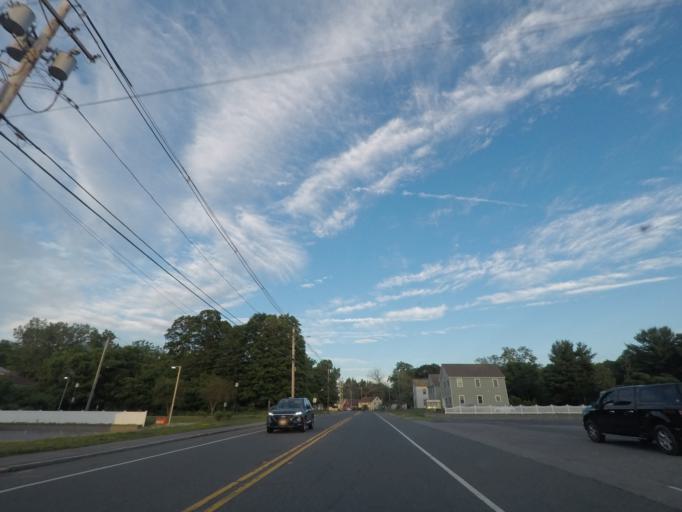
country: US
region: Massachusetts
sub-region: Worcester County
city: Warren
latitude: 42.2152
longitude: -72.2056
